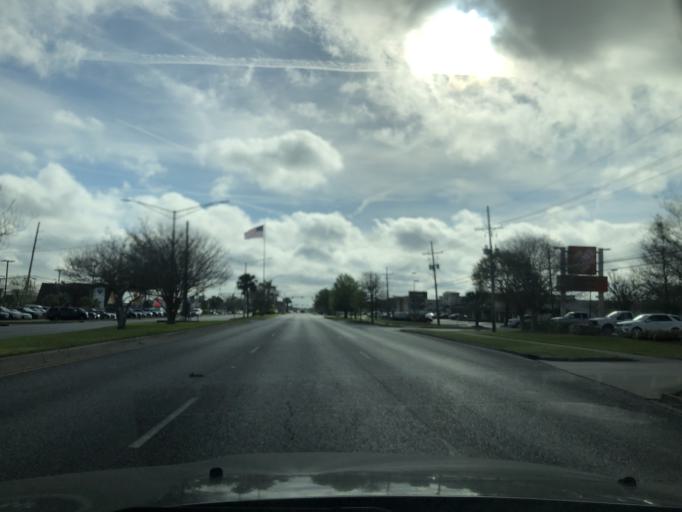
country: US
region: Louisiana
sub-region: Jefferson Parish
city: Kenner
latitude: 30.0060
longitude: -90.2323
